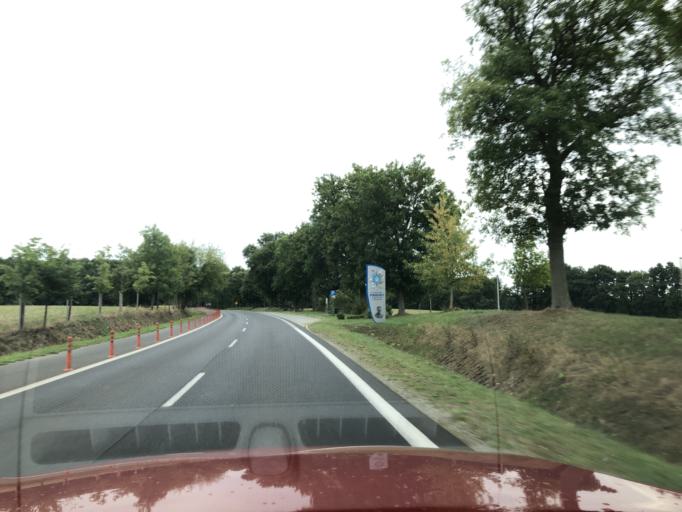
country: PL
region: Greater Poland Voivodeship
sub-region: Powiat szamotulski
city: Pniewy
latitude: 52.5171
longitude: 16.2360
